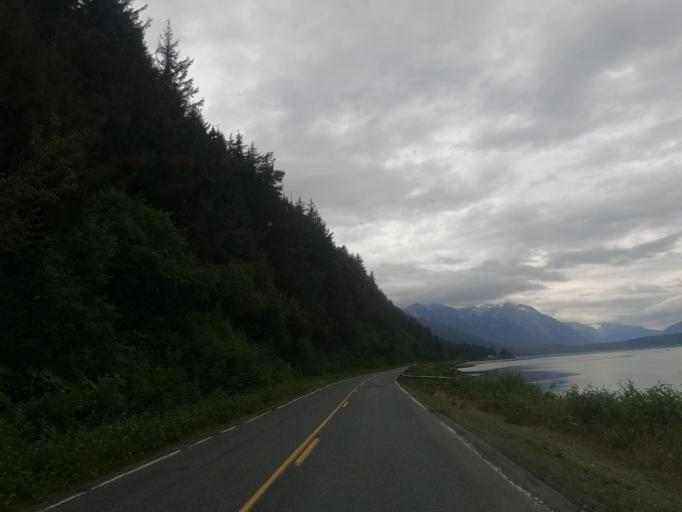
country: US
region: Alaska
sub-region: Haines Borough
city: Haines
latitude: 59.2912
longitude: -135.4955
